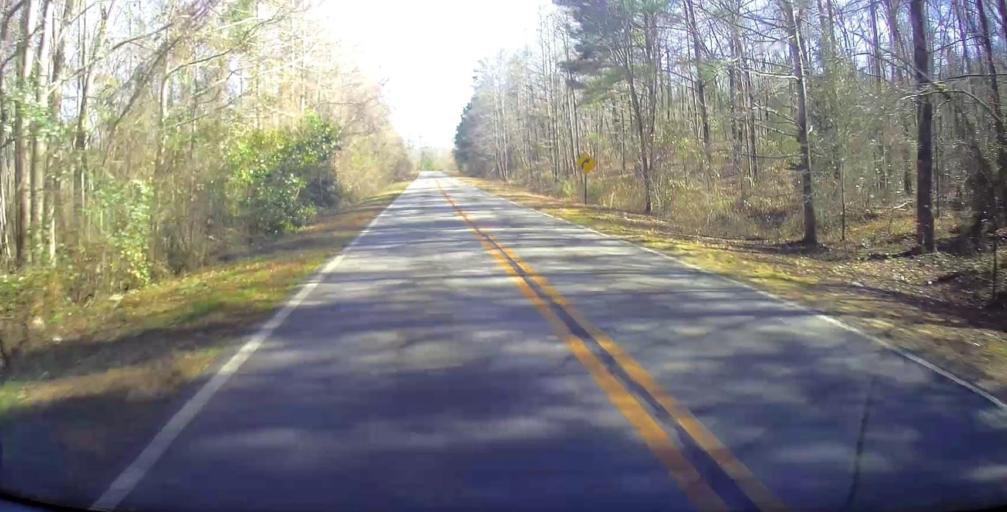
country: US
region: Georgia
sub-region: Peach County
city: Byron
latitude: 32.6098
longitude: -83.8056
